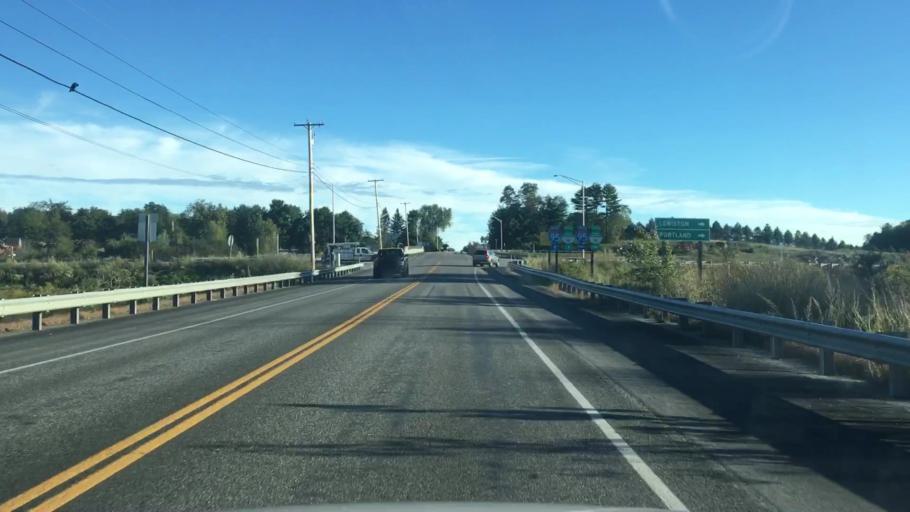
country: US
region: Maine
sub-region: Androscoggin County
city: Sabattus
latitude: 44.1027
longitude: -70.0865
